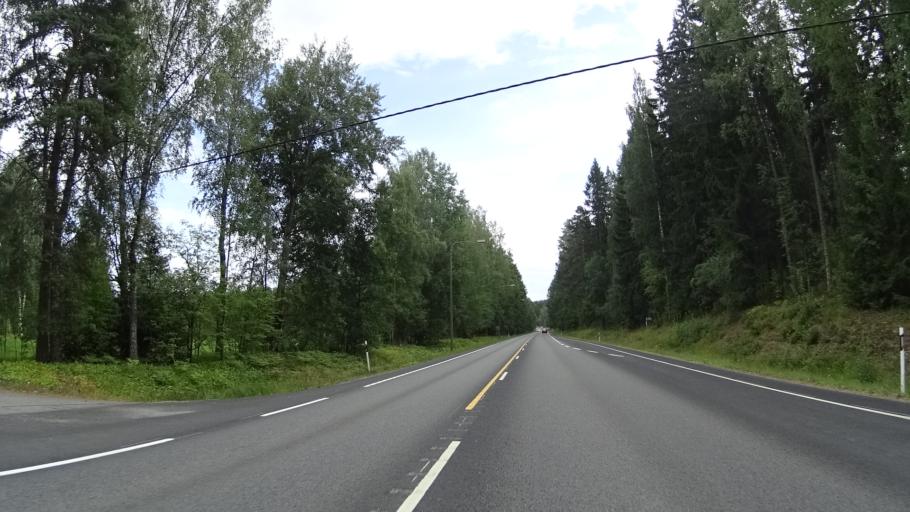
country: FI
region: Pirkanmaa
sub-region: Tampere
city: Kangasala
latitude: 61.4260
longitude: 24.1352
